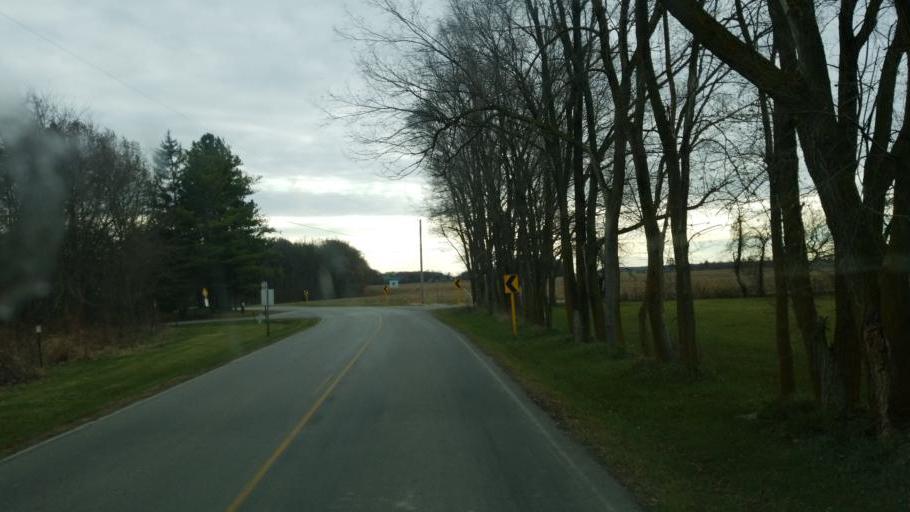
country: US
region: Ohio
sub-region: Wyandot County
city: Upper Sandusky
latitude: 40.7029
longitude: -83.2479
